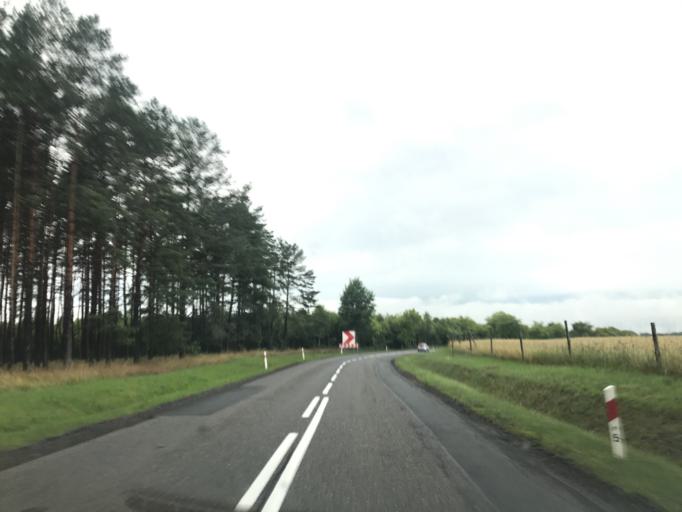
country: PL
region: Pomeranian Voivodeship
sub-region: Powiat czluchowski
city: Czarne
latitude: 53.8210
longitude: 16.9511
